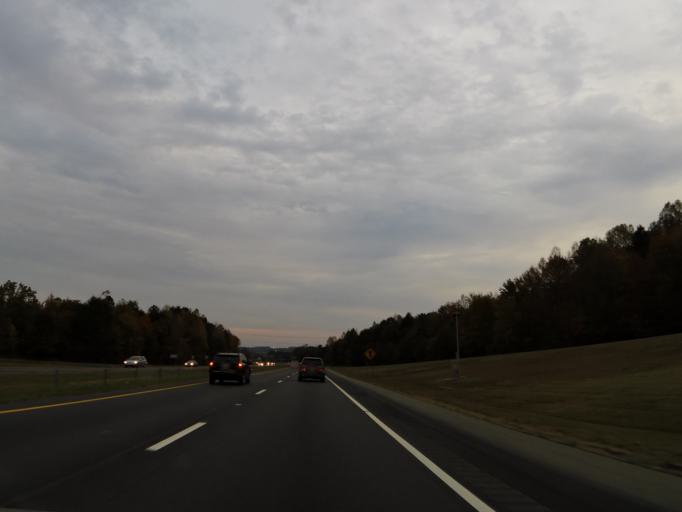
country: US
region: North Carolina
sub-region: Catawba County
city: Hickory
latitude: 35.7208
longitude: -81.3562
